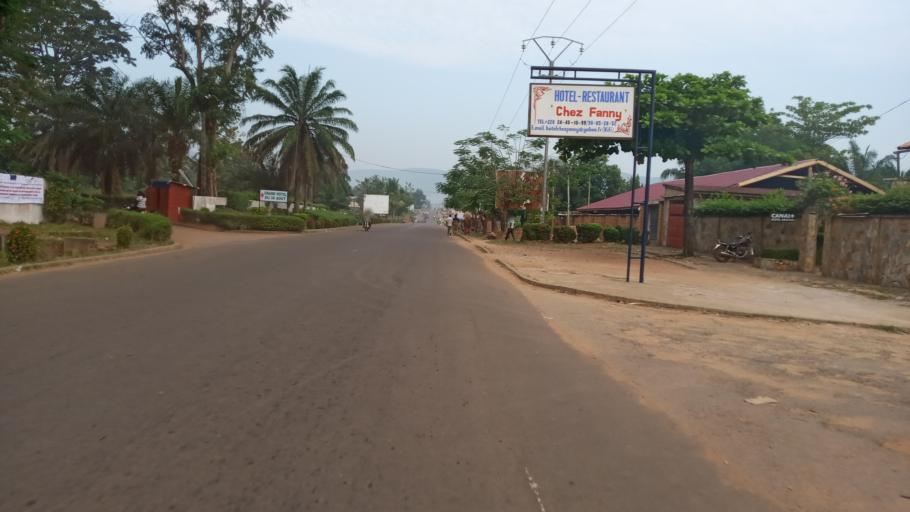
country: TG
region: Plateaux
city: Kpalime
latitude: 6.8920
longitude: 0.6407
